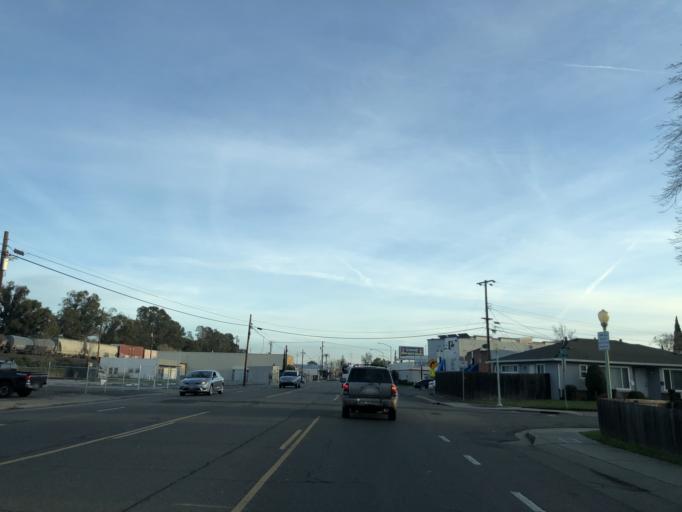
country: US
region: California
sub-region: Sacramento County
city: Rosemont
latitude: 38.5578
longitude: -121.4282
